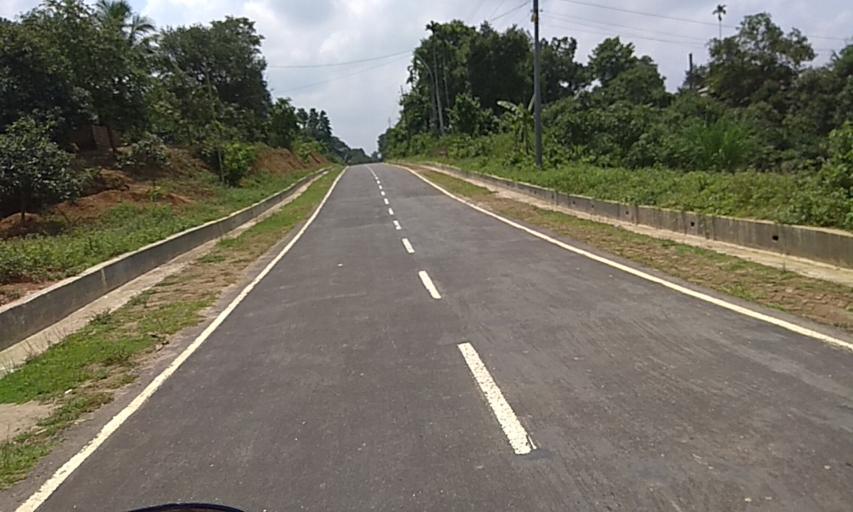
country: BD
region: Chittagong
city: Manikchari
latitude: 22.9381
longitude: 91.8908
